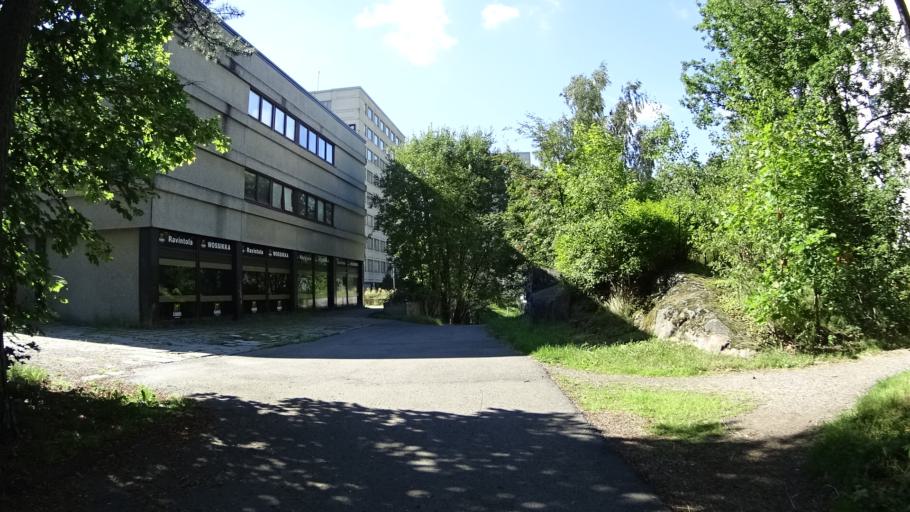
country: FI
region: Uusimaa
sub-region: Helsinki
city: Teekkarikylae
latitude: 60.2254
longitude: 24.8590
